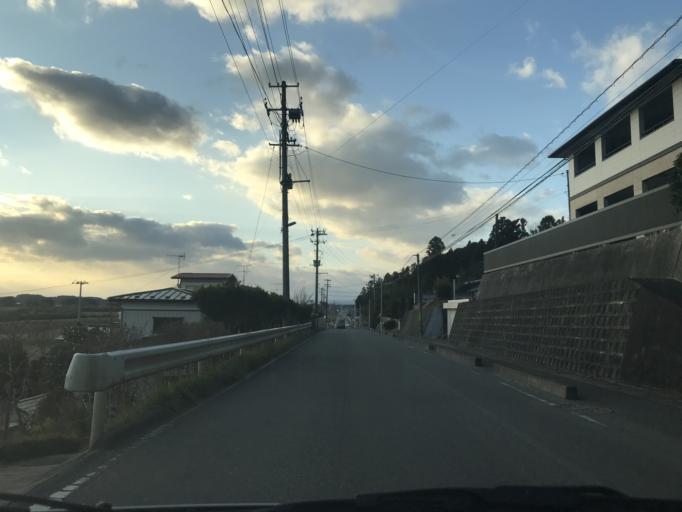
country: JP
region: Miyagi
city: Kogota
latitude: 38.6529
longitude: 141.0596
